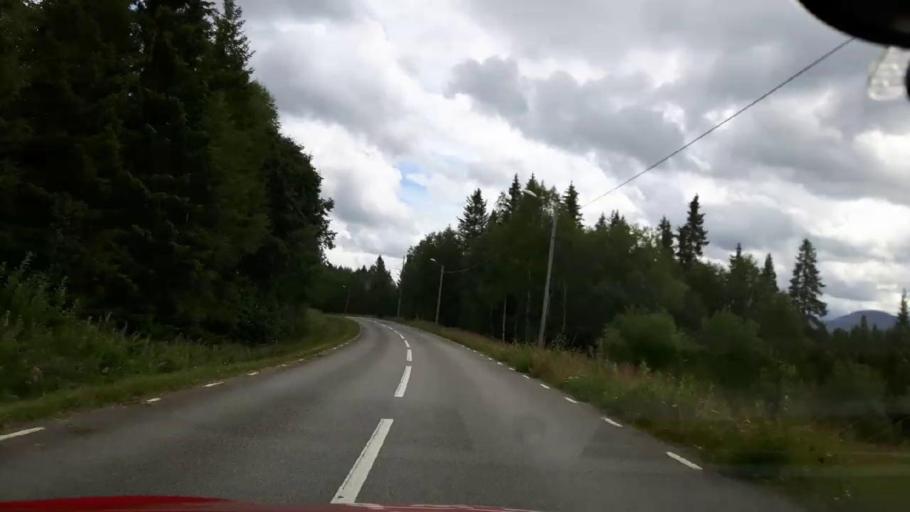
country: NO
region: Nord-Trondelag
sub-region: Lierne
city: Sandvika
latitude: 64.3906
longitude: 14.3762
